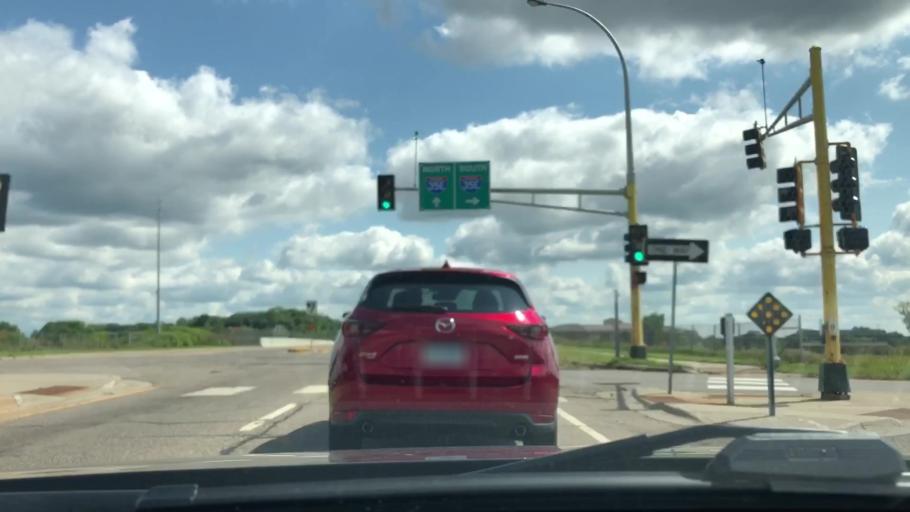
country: US
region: Minnesota
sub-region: Dakota County
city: Mendota Heights
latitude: 44.8479
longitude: -93.1552
